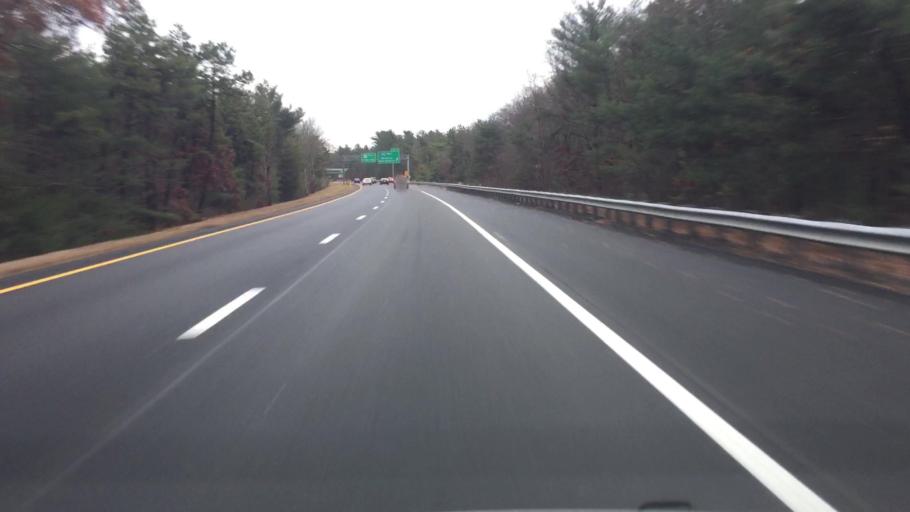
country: US
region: Massachusetts
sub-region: Plymouth County
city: West Wareham
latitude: 41.7862
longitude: -70.7379
